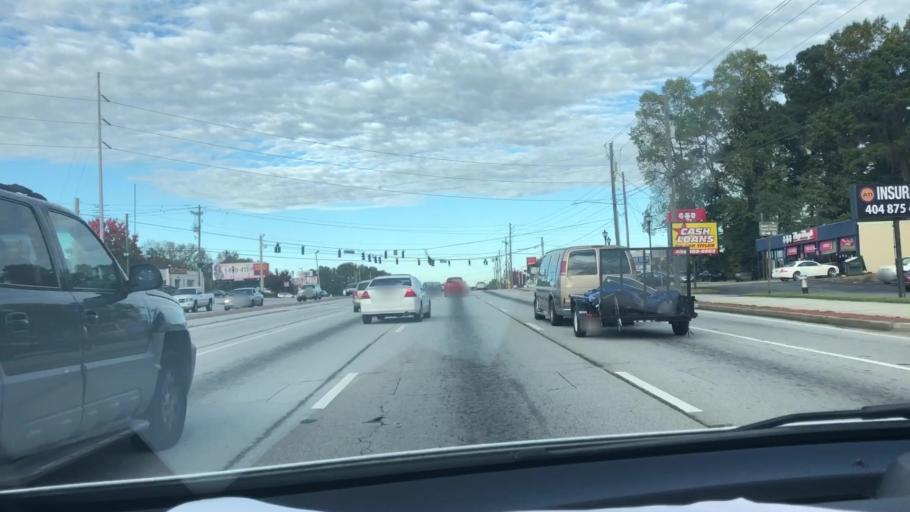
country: US
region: Georgia
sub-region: DeKalb County
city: Clarkston
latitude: 33.7858
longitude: -84.2344
